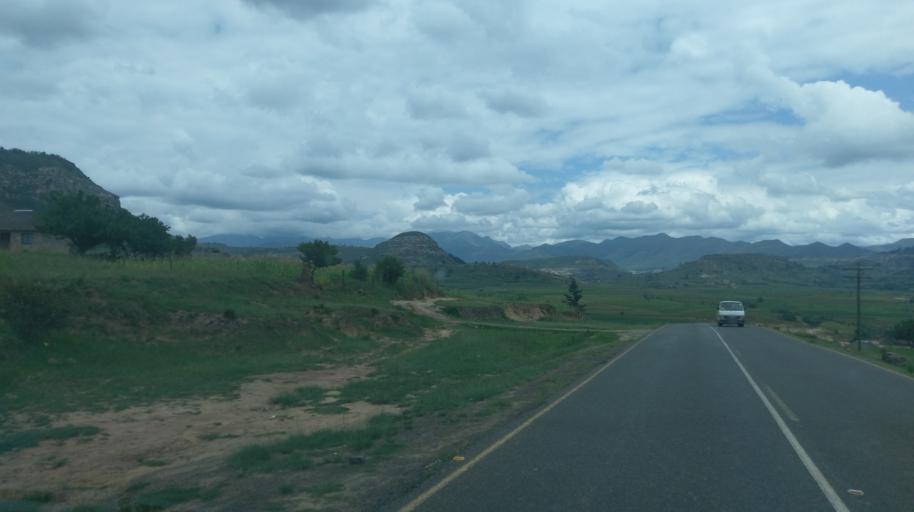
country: LS
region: Leribe
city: Leribe
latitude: -28.9674
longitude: 28.1727
